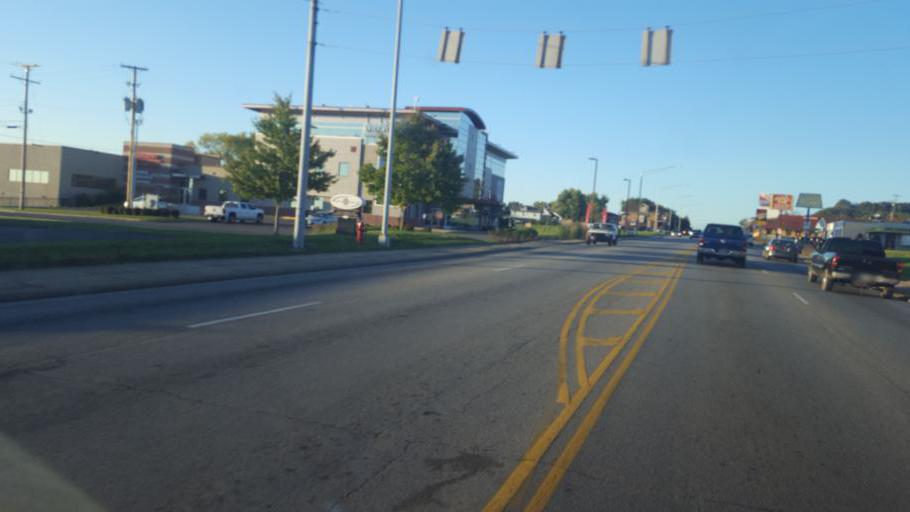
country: US
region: Ohio
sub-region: Scioto County
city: Portsmouth
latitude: 38.7475
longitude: -82.9922
